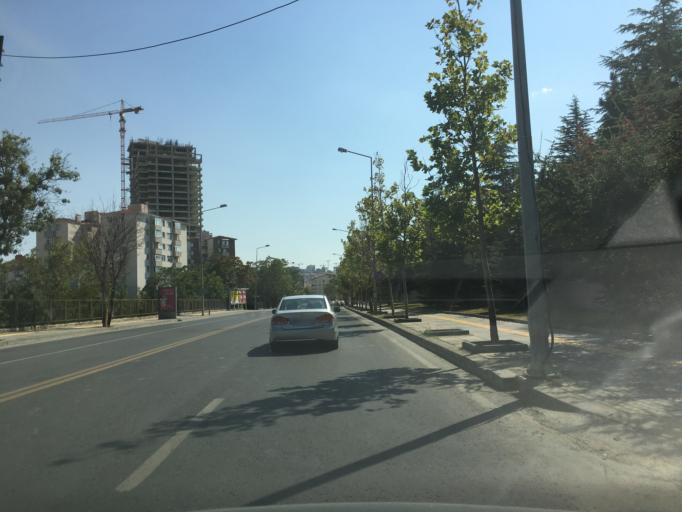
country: TR
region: Ankara
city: Cankaya
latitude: 39.8814
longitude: 32.8663
